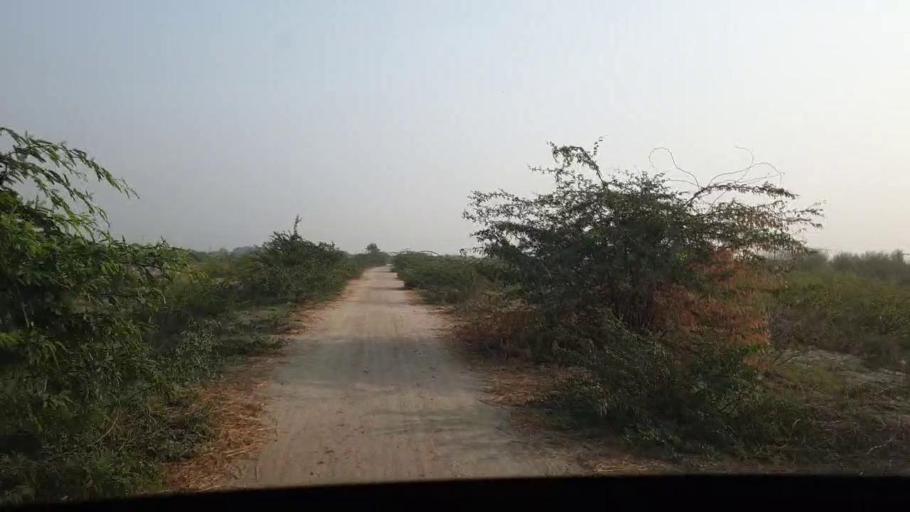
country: PK
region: Sindh
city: Jati
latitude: 24.2596
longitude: 68.1187
